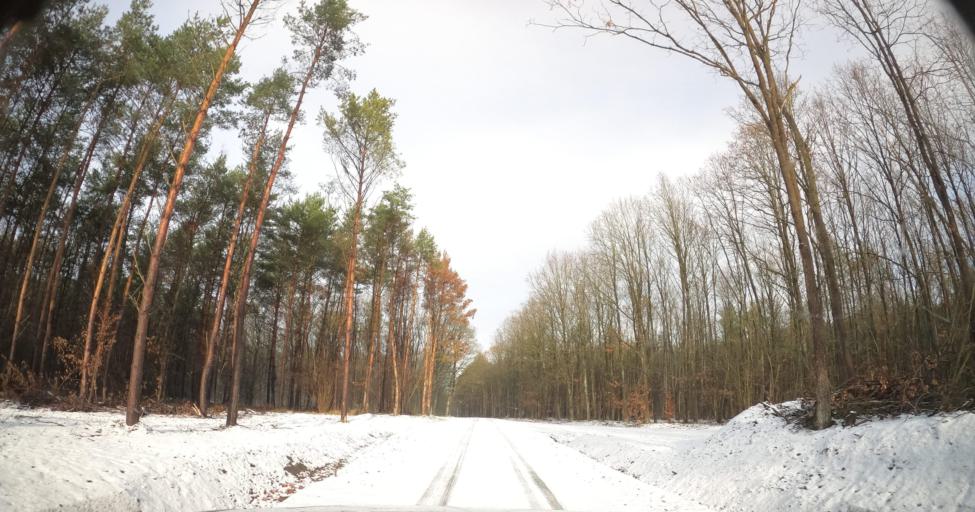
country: PL
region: West Pomeranian Voivodeship
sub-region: Powiat gryfinski
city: Mieszkowice
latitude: 52.7322
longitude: 14.4900
